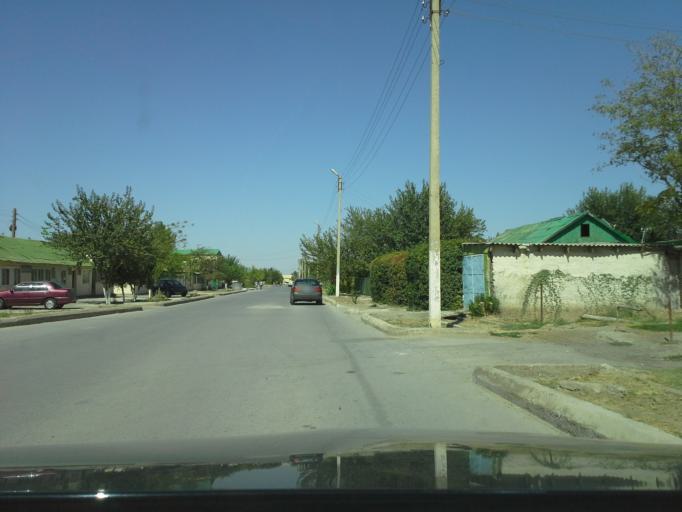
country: TM
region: Ahal
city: Ashgabat
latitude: 38.0039
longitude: 58.3014
